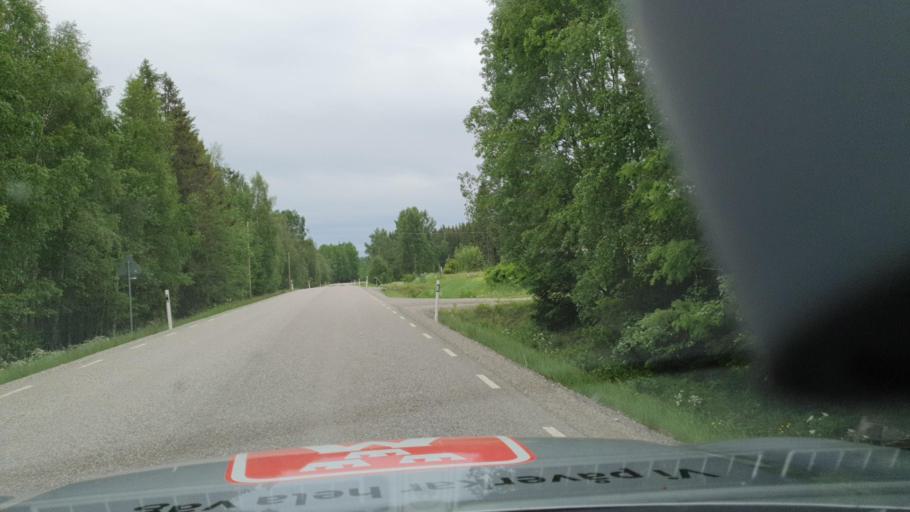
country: SE
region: Vaesternorrland
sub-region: Kramfors Kommun
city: Kramfors
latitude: 62.9506
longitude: 17.9030
